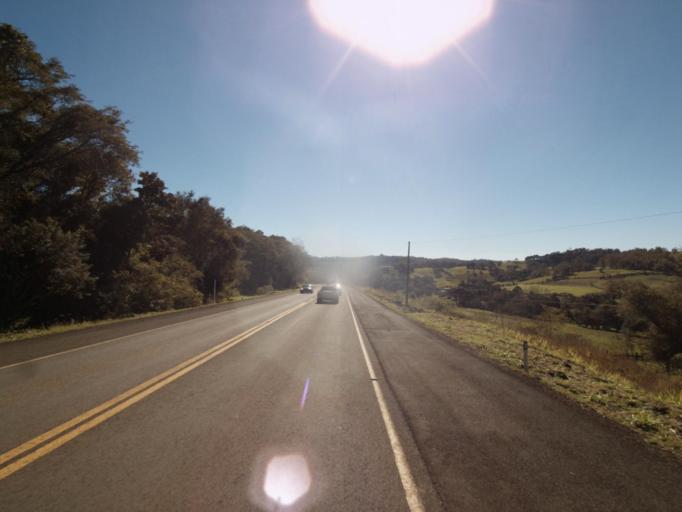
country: AR
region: Misiones
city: Bernardo de Irigoyen
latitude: -26.6948
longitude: -53.5385
